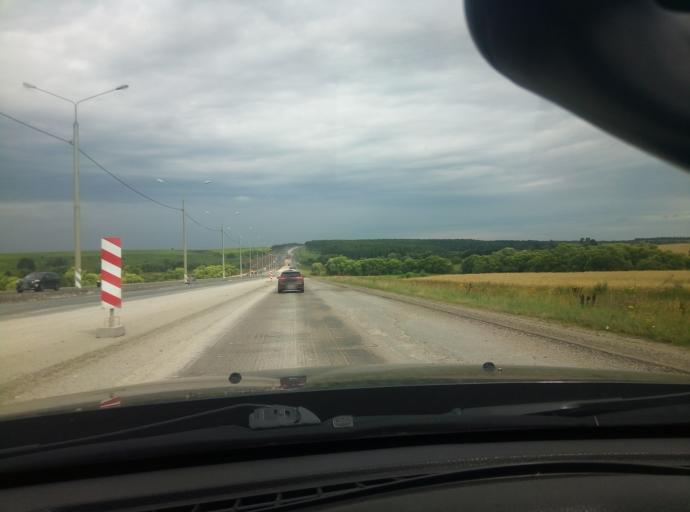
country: RU
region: Tula
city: Novogurovskiy
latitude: 54.4896
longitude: 37.5124
